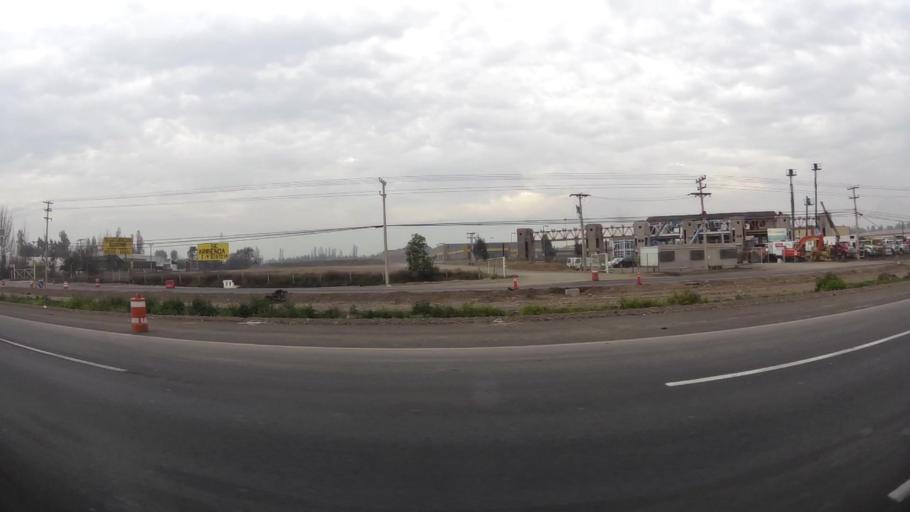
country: CL
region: Santiago Metropolitan
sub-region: Provincia de Chacabuco
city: Chicureo Abajo
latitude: -33.2905
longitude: -70.7342
